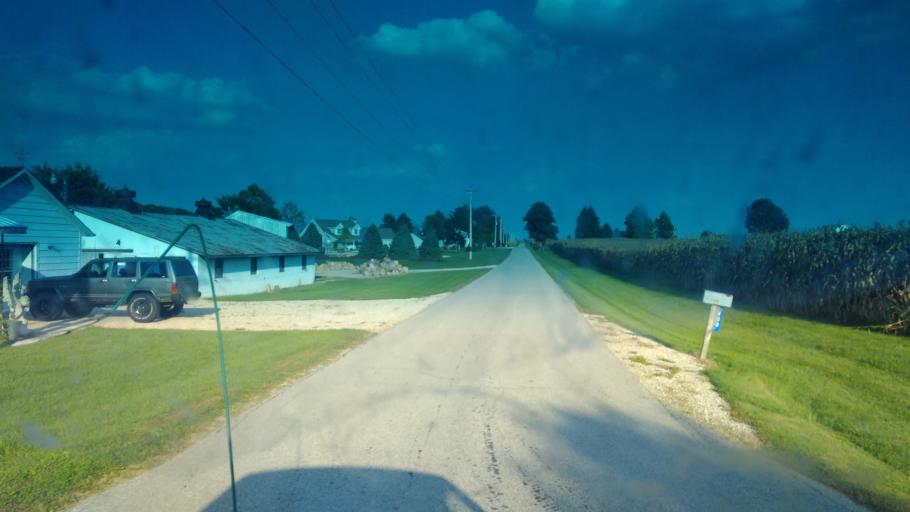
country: US
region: Ohio
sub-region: Seneca County
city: Tiffin
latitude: 40.9646
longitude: -83.0934
